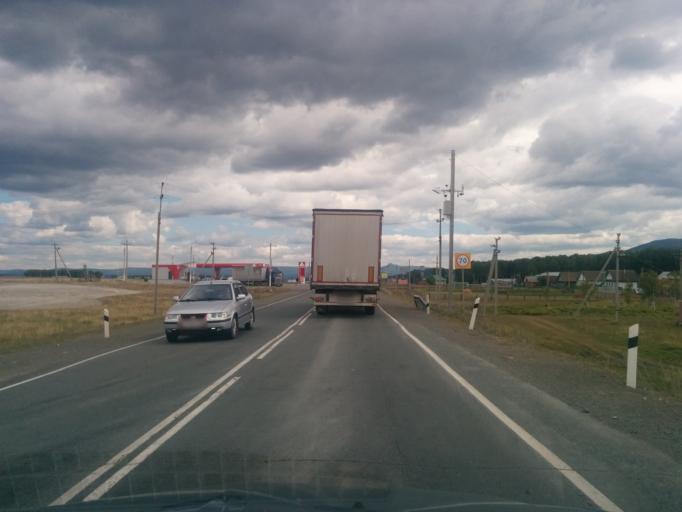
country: RU
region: Bashkortostan
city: Lomovka
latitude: 53.8825
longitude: 58.1023
